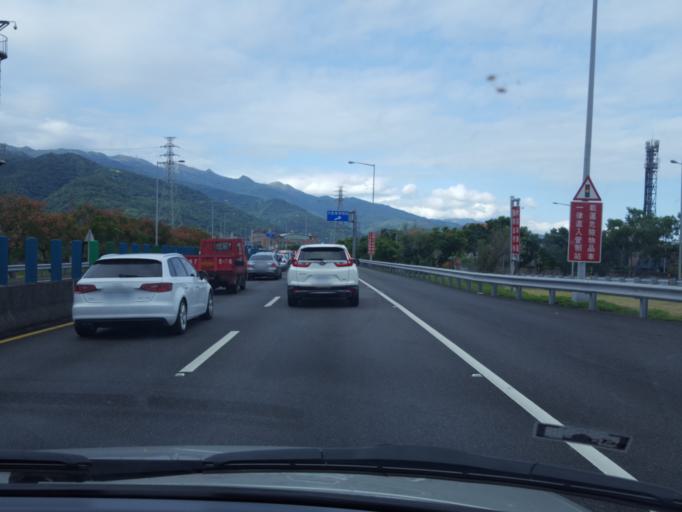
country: TW
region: Taiwan
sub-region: Yilan
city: Yilan
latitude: 24.8285
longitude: 121.7902
